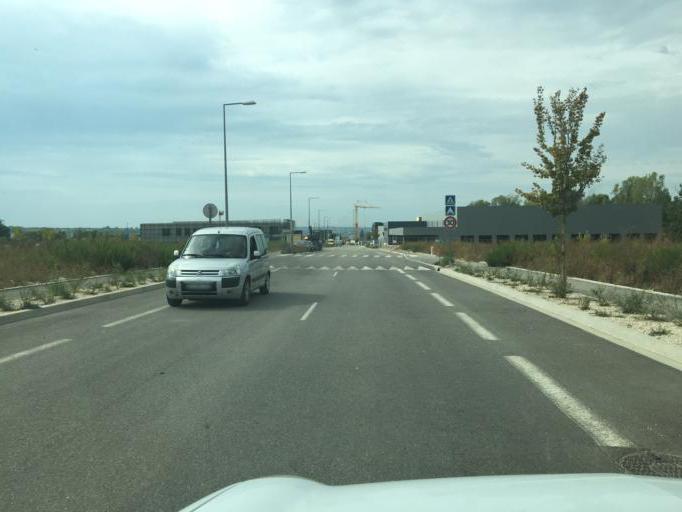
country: FR
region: Provence-Alpes-Cote d'Azur
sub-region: Departement des Bouches-du-Rhone
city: Bouc-Bel-Air
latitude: 43.4804
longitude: 5.3936
